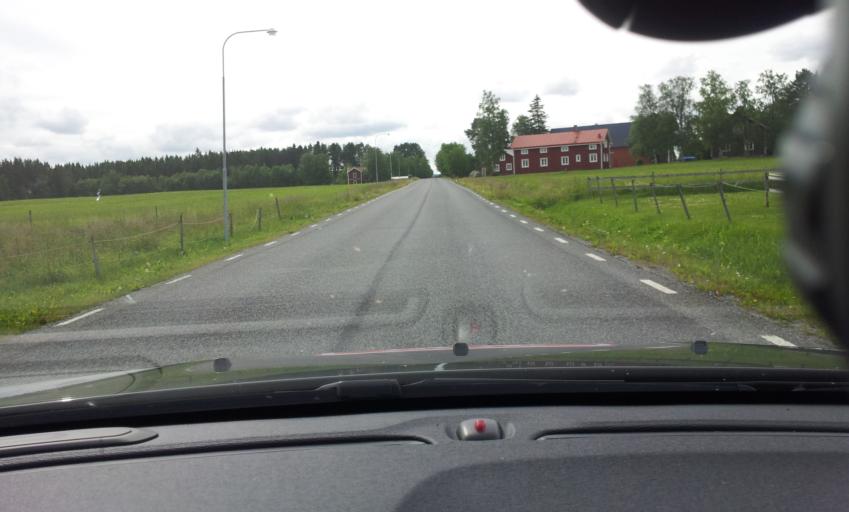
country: SE
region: Jaemtland
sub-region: OEstersunds Kommun
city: Brunflo
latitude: 63.0247
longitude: 14.8686
